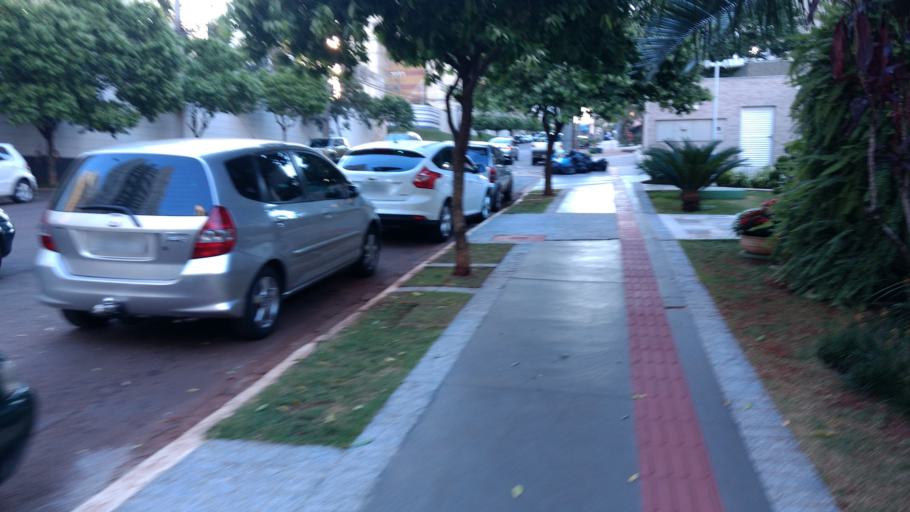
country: BR
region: Parana
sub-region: Londrina
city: Londrina
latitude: -23.3323
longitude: -51.1754
